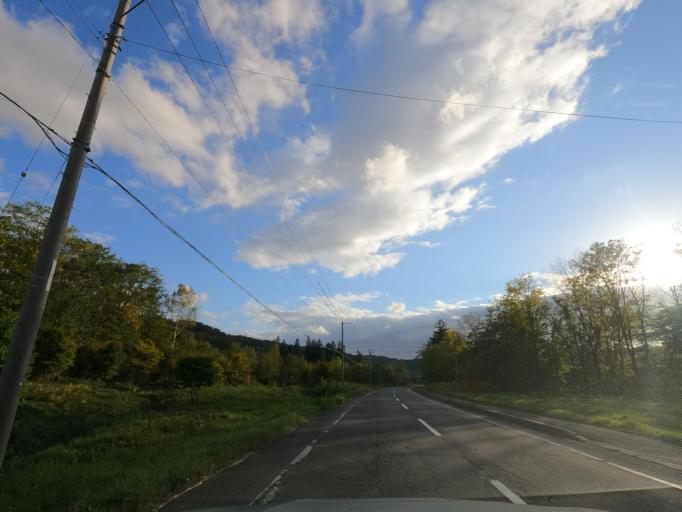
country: JP
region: Hokkaido
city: Date
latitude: 42.6437
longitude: 141.0517
